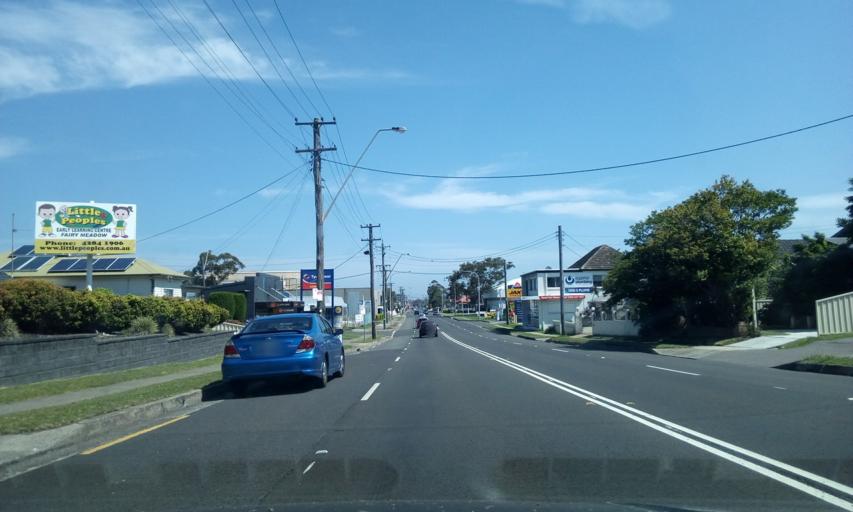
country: AU
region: New South Wales
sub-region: Wollongong
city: Corrimal
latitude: -34.3851
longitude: 150.8946
